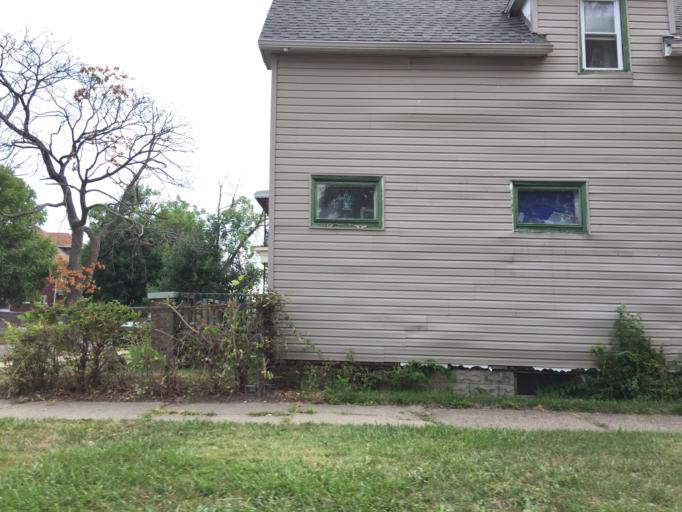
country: US
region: Michigan
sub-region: Wayne County
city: Highland Park
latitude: 42.3727
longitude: -83.0897
